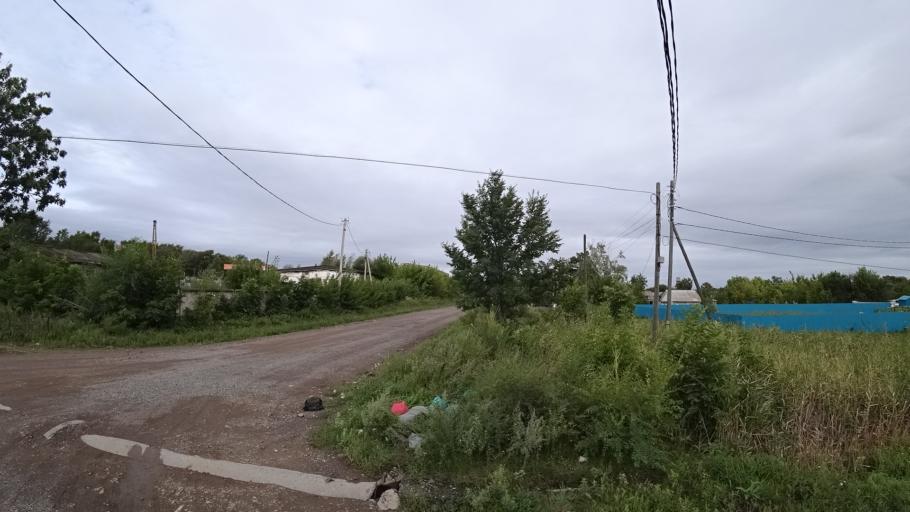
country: RU
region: Primorskiy
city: Chernigovka
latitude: 44.3327
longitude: 132.5754
